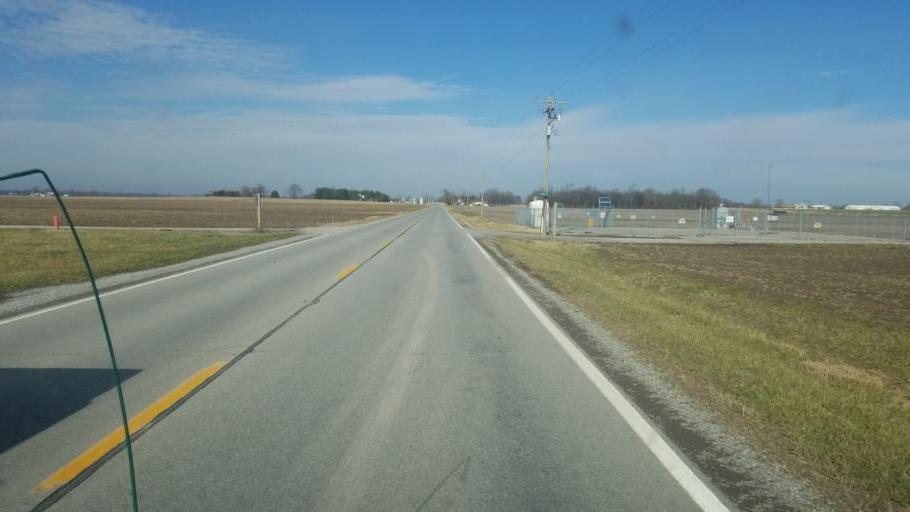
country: US
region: Illinois
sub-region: Saline County
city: Eldorado
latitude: 37.8921
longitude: -88.4530
